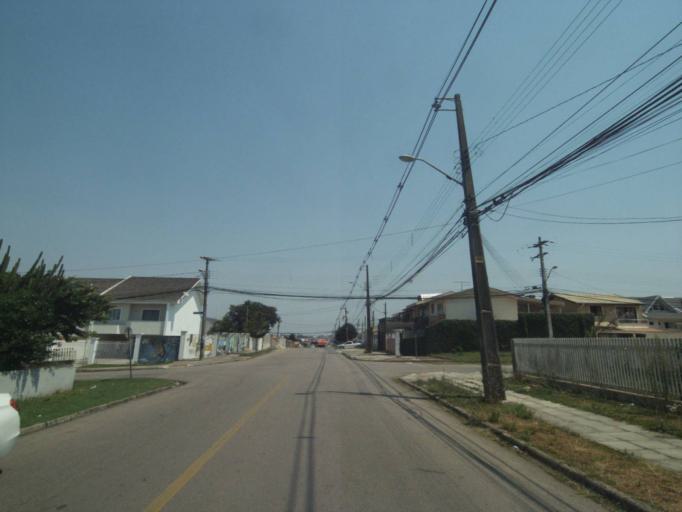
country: BR
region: Parana
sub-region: Sao Jose Dos Pinhais
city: Sao Jose dos Pinhais
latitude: -25.5100
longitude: -49.2640
